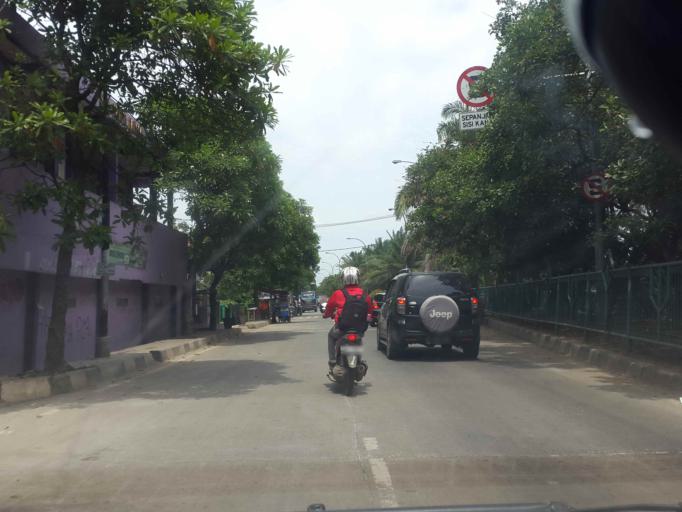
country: ID
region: Banten
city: Tangerang
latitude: -6.1545
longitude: 106.6324
